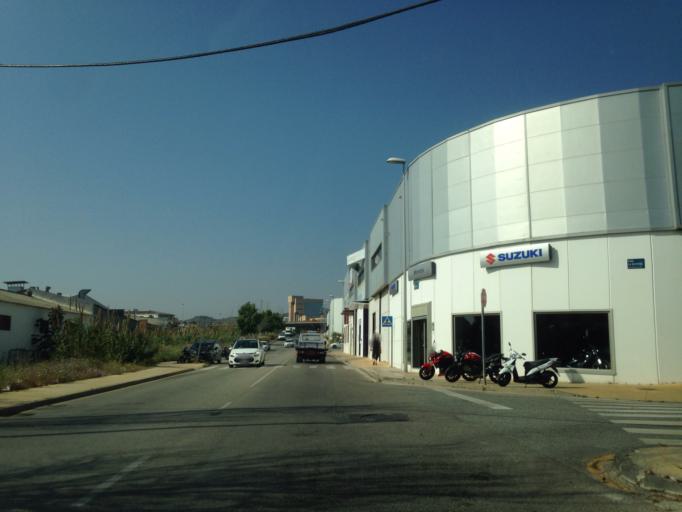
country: ES
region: Andalusia
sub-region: Provincia de Malaga
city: Malaga
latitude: 36.7107
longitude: -4.4723
